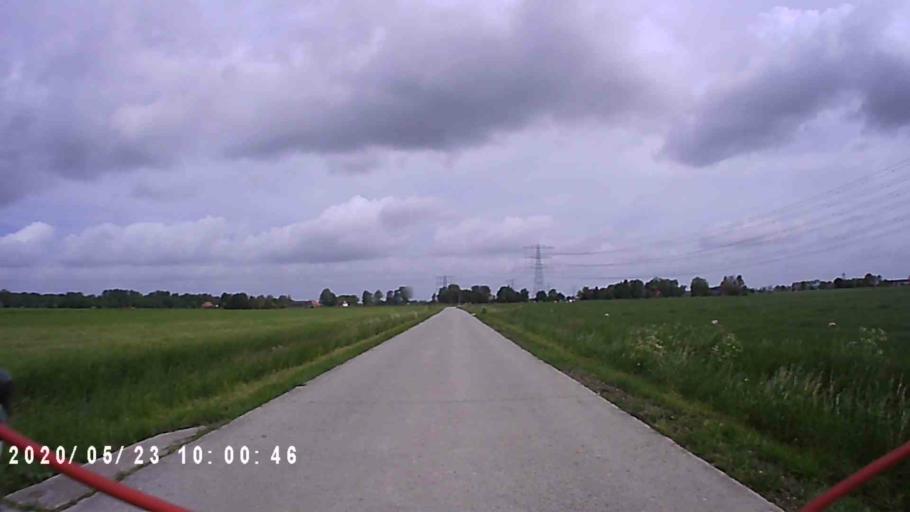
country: NL
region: Groningen
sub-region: Gemeente Appingedam
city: Appingedam
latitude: 53.3133
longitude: 6.8204
